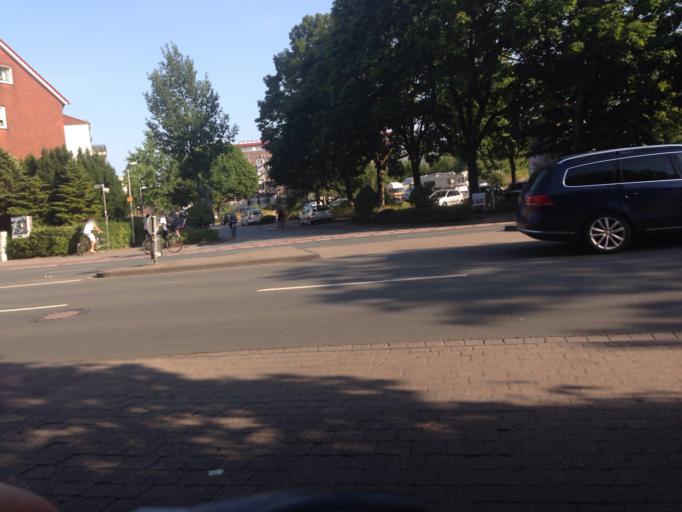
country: DE
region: North Rhine-Westphalia
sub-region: Regierungsbezirk Munster
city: Muenster
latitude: 51.9742
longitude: 7.6079
